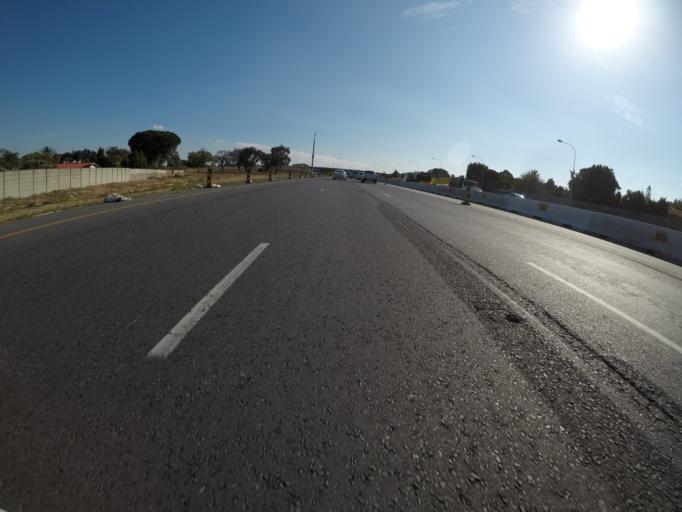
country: ZA
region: Western Cape
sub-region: City of Cape Town
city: Kraaifontein
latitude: -33.8757
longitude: 18.6621
